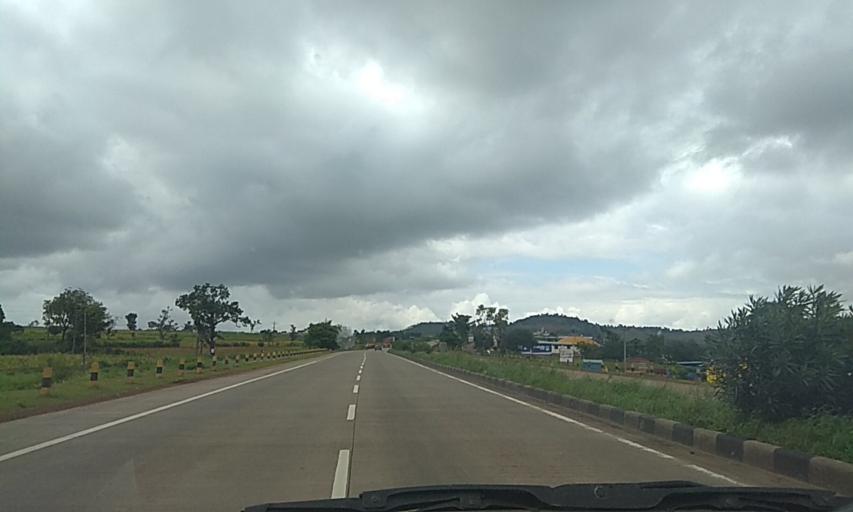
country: IN
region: Karnataka
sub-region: Belgaum
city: Sankeshwar
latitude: 16.2562
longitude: 74.4698
